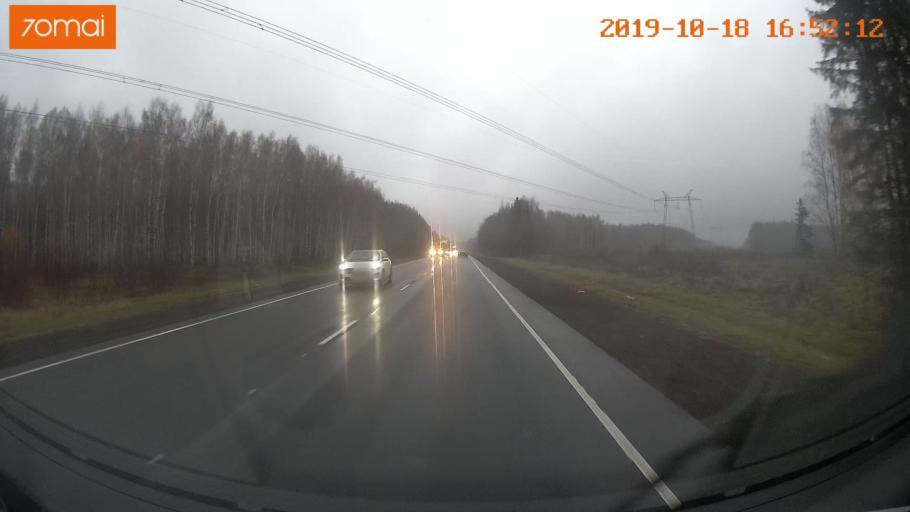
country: RU
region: Vladimir
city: Kideksha
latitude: 56.5970
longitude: 40.5557
